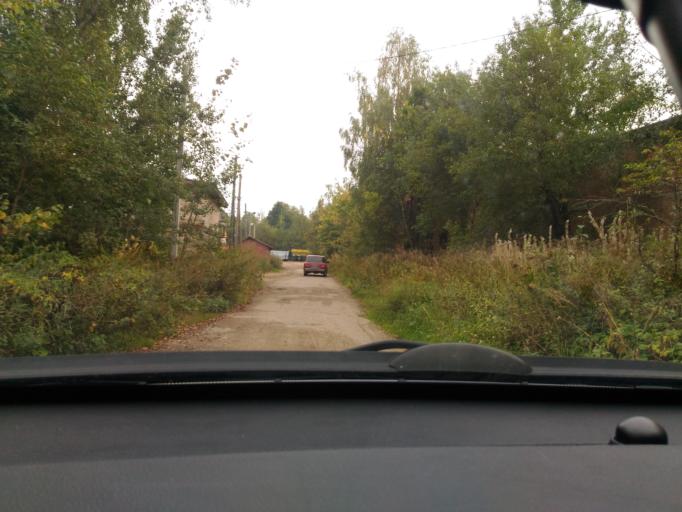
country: RU
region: Moskovskaya
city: Povarovo
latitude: 56.0913
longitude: 37.0618
